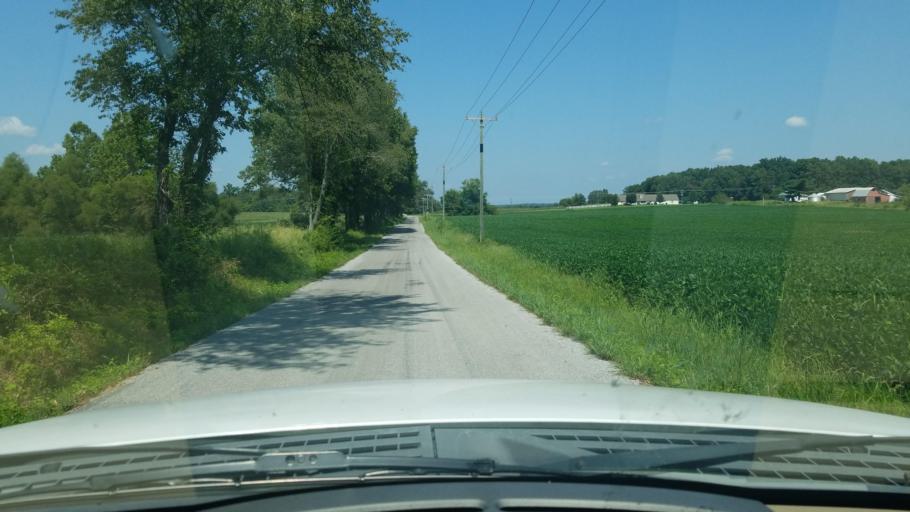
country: US
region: Illinois
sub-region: Saline County
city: Harrisburg
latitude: 37.8013
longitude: -88.6240
